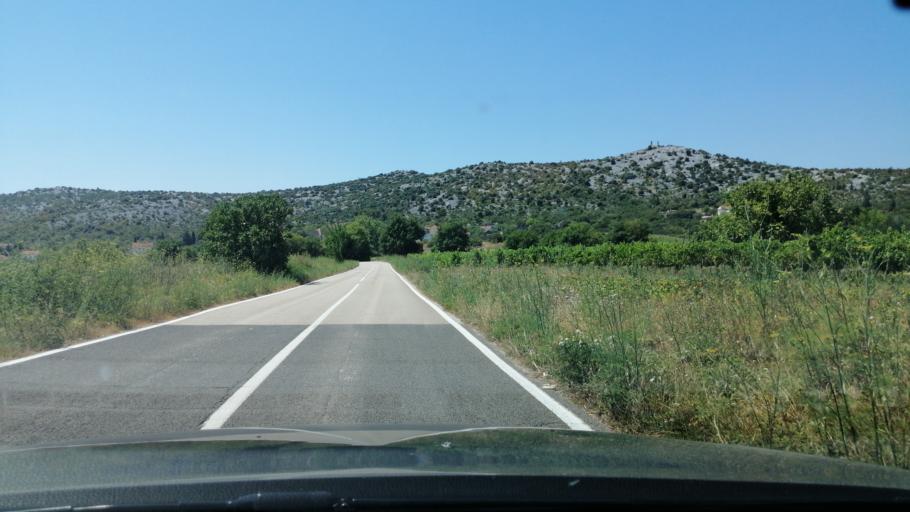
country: HR
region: Sibensko-Kniniska
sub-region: Grad Sibenik
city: Pirovac
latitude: 43.8759
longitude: 15.6815
